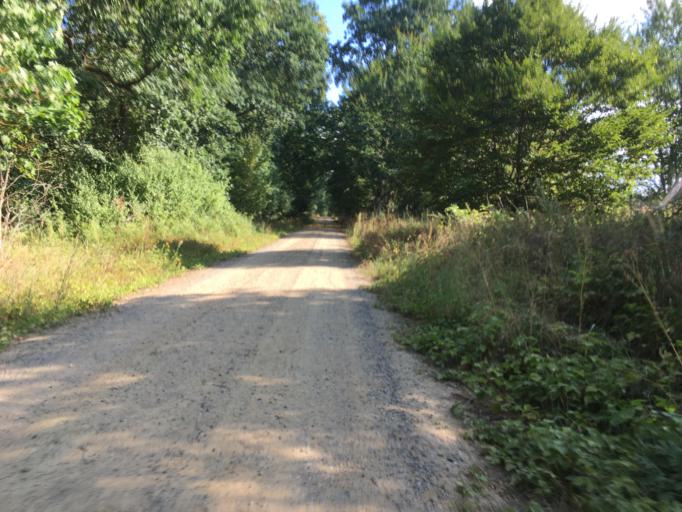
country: DE
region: Brandenburg
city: Liebenwalde
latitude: 52.9195
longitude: 13.4329
